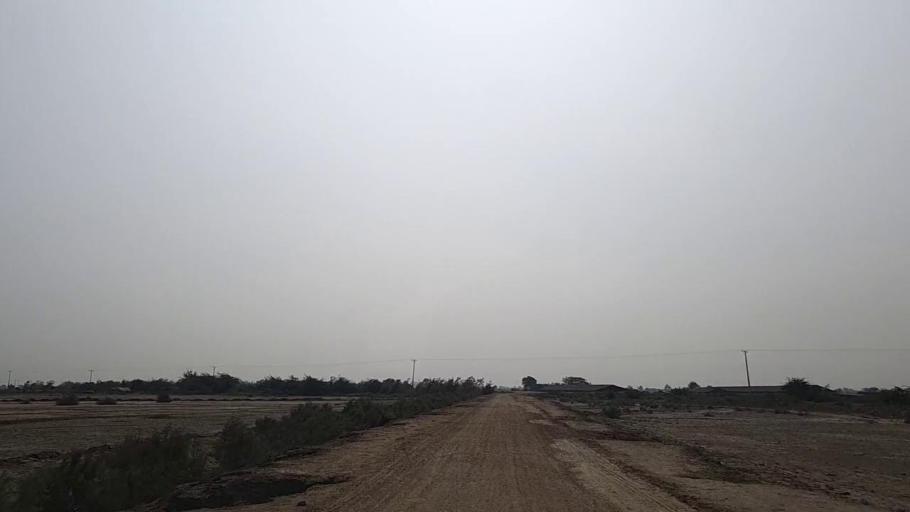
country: PK
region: Sindh
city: Mirpur Sakro
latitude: 24.6308
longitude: 67.7678
